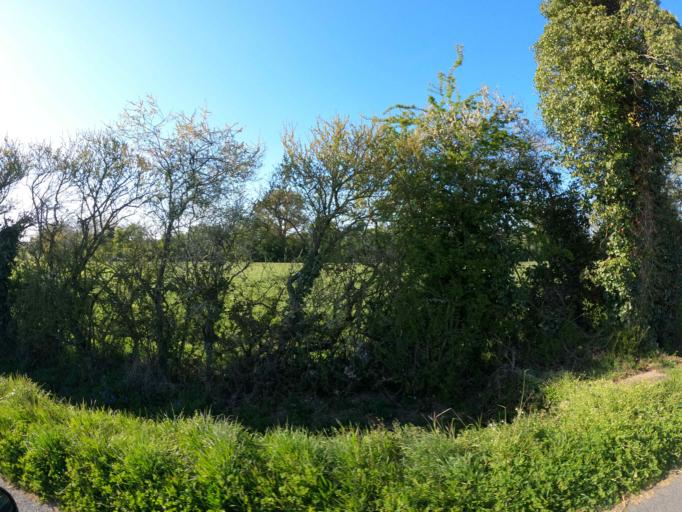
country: FR
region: Pays de la Loire
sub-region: Departement de la Vendee
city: Les Brouzils
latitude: 46.8910
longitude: -1.3073
